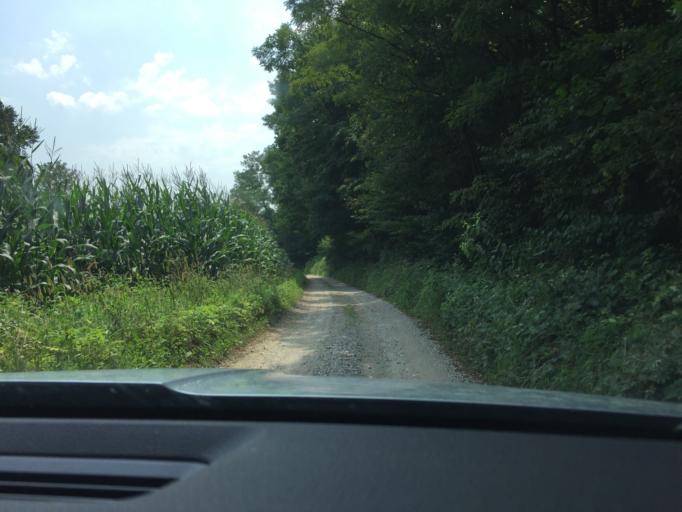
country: SI
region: Metlika
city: Metlika
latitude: 45.6528
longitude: 15.3464
